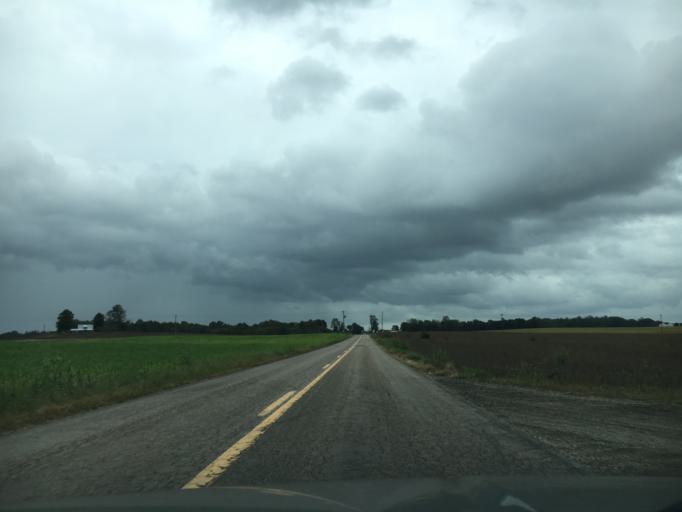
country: US
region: Virginia
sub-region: Amelia County
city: Amelia Court House
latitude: 37.4001
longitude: -77.9692
